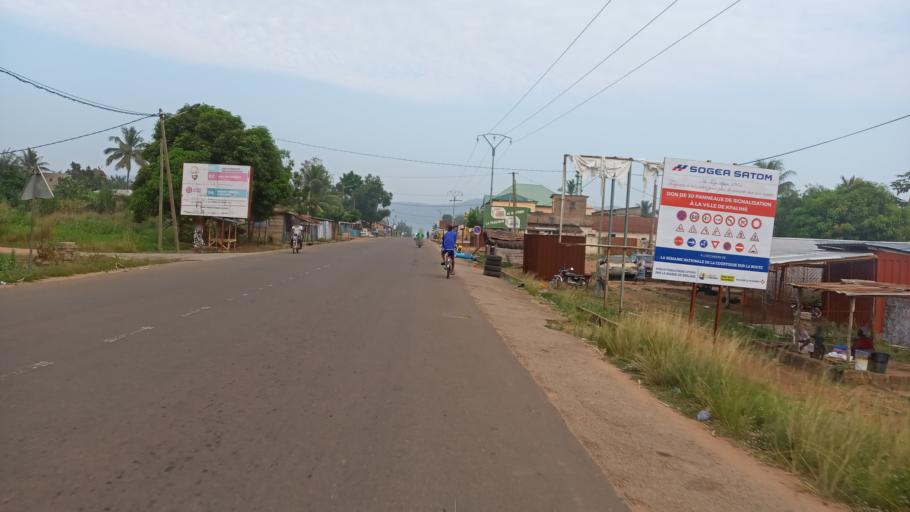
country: TG
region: Plateaux
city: Kpalime
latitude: 6.8939
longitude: 0.6393
